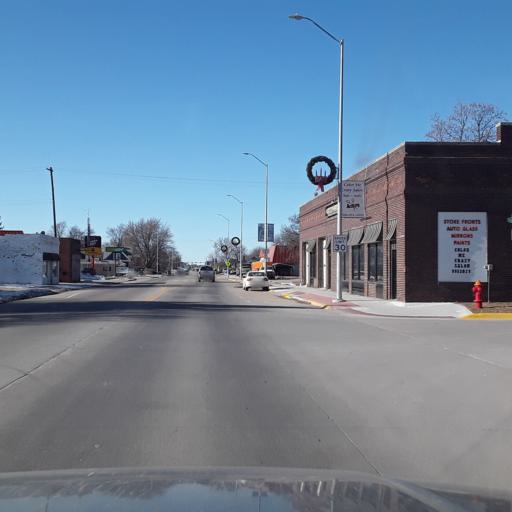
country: US
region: Nebraska
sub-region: Phelps County
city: Holdrege
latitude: 40.4380
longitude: -99.3735
